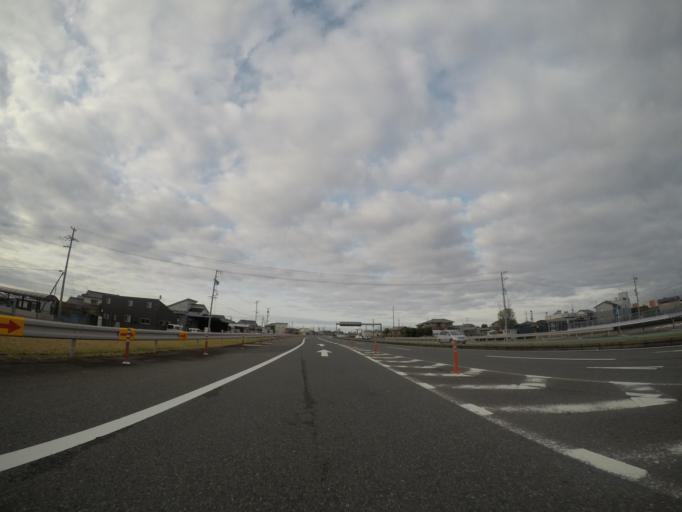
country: JP
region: Shizuoka
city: Hamakita
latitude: 34.8287
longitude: 137.8113
